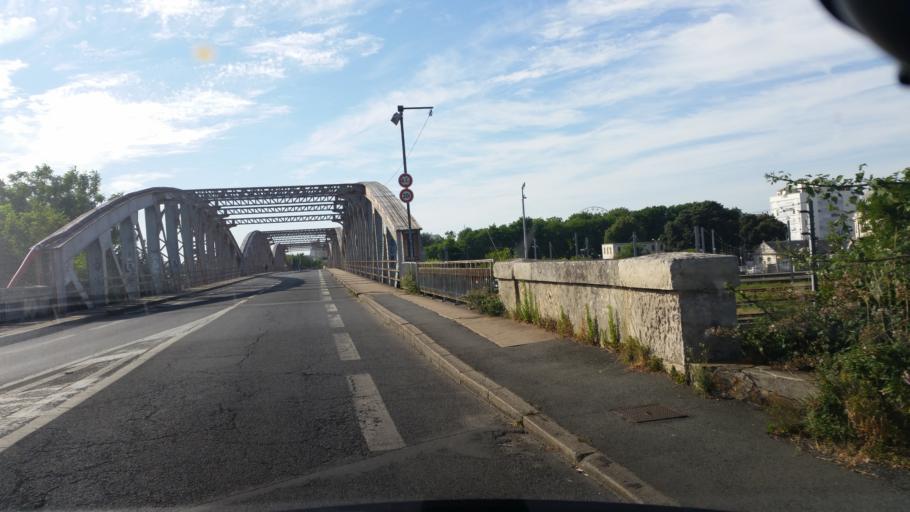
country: FR
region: Poitou-Charentes
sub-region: Departement de la Charente-Maritime
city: La Rochelle
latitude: 46.1506
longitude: -1.1462
